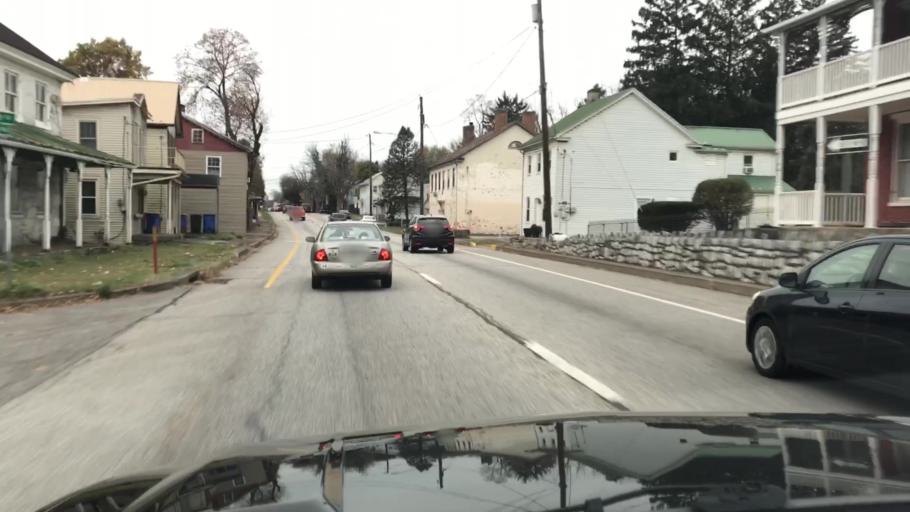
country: US
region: Pennsylvania
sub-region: Cumberland County
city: Mechanicsburg
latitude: 40.2456
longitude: -77.0338
